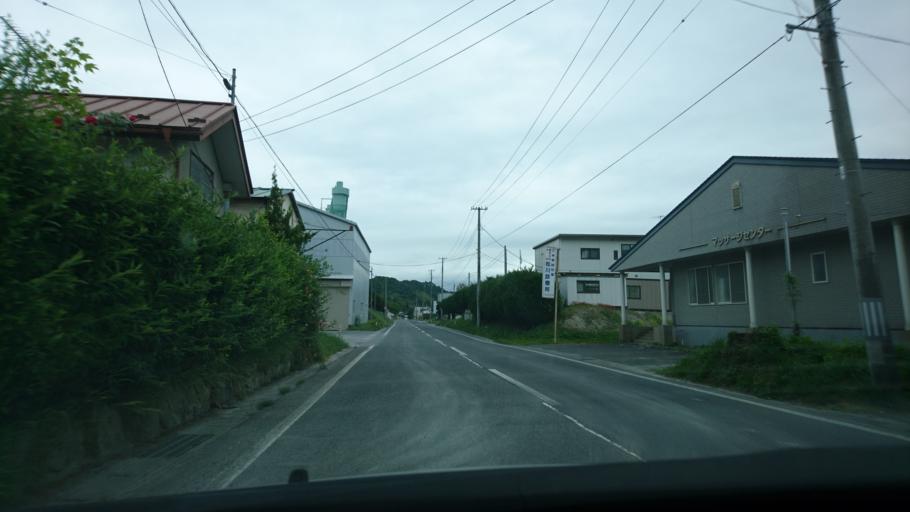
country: JP
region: Iwate
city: Ichinoseki
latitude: 38.9754
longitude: 141.2381
